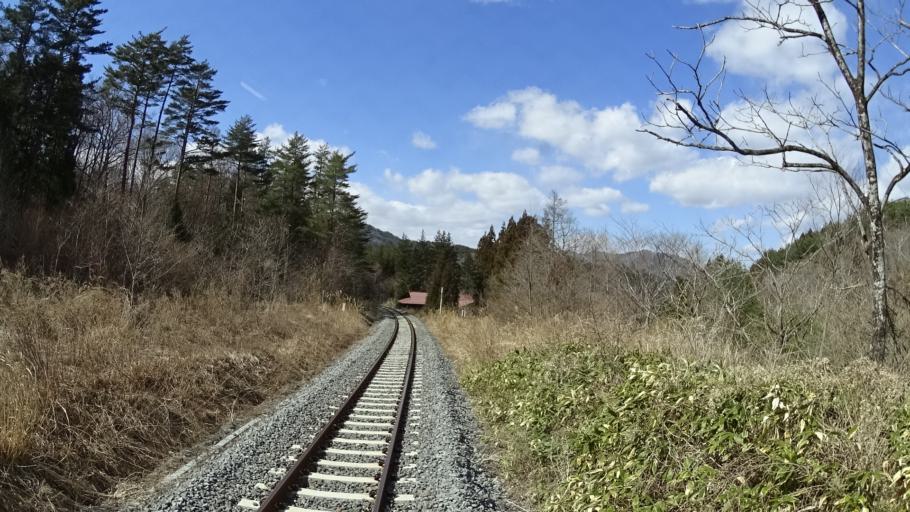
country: JP
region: Iwate
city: Yamada
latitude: 39.5076
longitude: 141.9206
